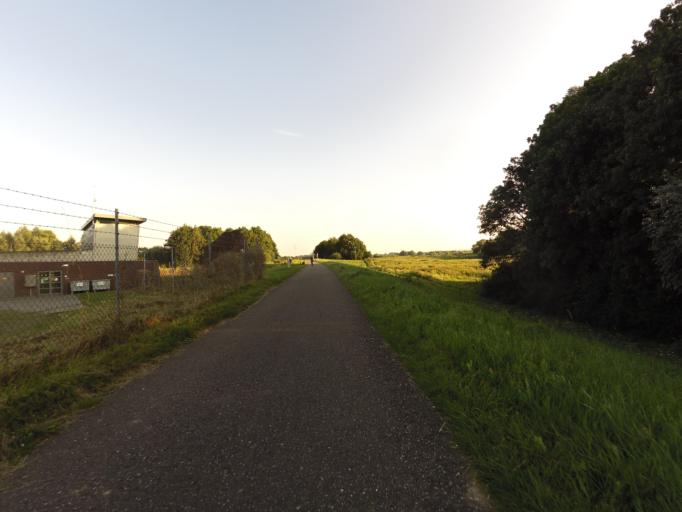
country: NL
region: Gelderland
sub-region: Gemeente Duiven
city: Duiven
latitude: 51.9169
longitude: 5.9967
